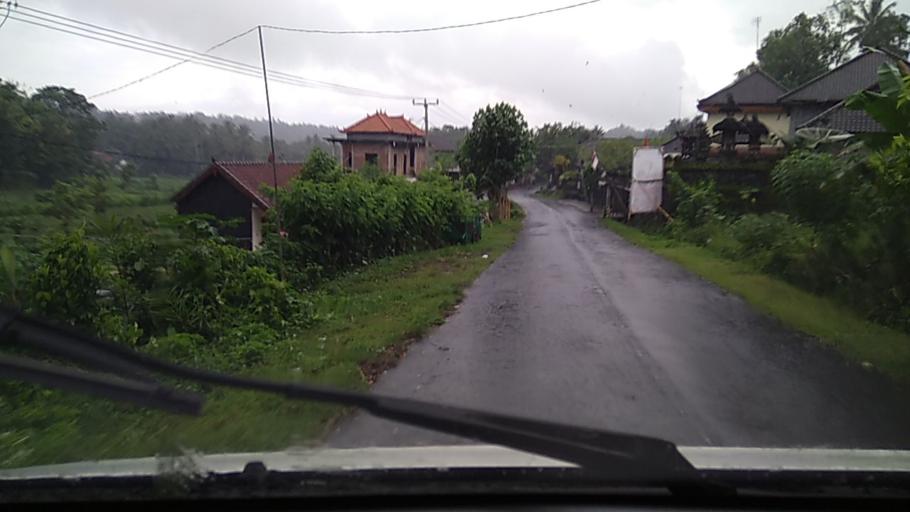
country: ID
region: Bali
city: Tiyingtali Kelod
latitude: -8.4105
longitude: 115.6163
